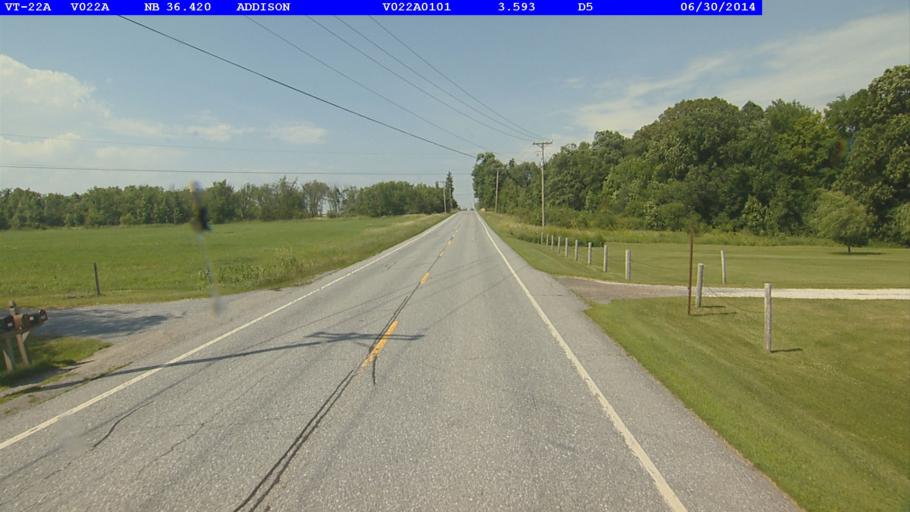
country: US
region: Vermont
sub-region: Addison County
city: Vergennes
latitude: 44.0813
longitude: -73.3031
